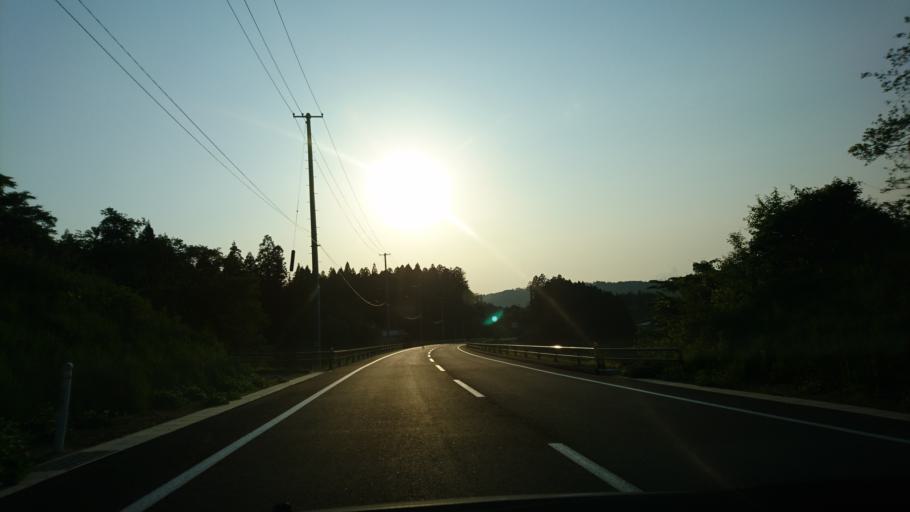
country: JP
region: Iwate
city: Ofunato
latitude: 38.9319
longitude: 141.4448
